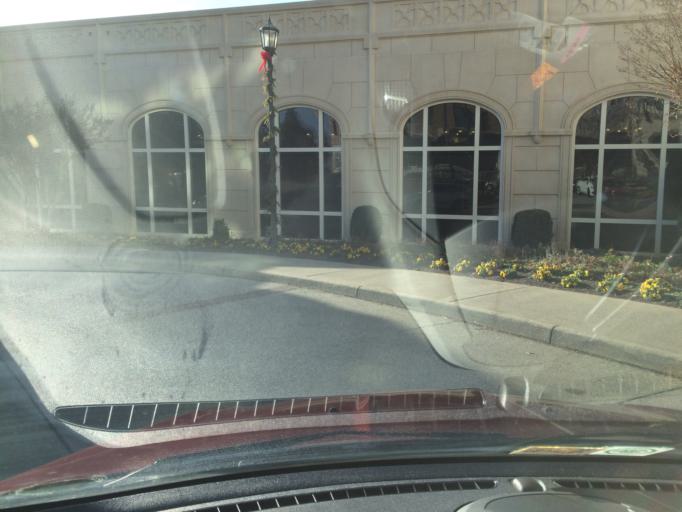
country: US
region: Virginia
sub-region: City of Roanoke
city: Roanoke
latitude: 37.2744
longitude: -79.9397
